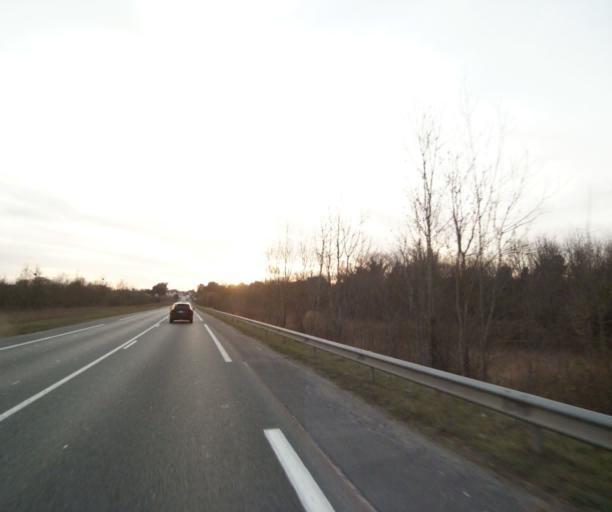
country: FR
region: Poitou-Charentes
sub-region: Departement de la Charente-Maritime
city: Saintes
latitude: 45.7288
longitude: -0.6324
